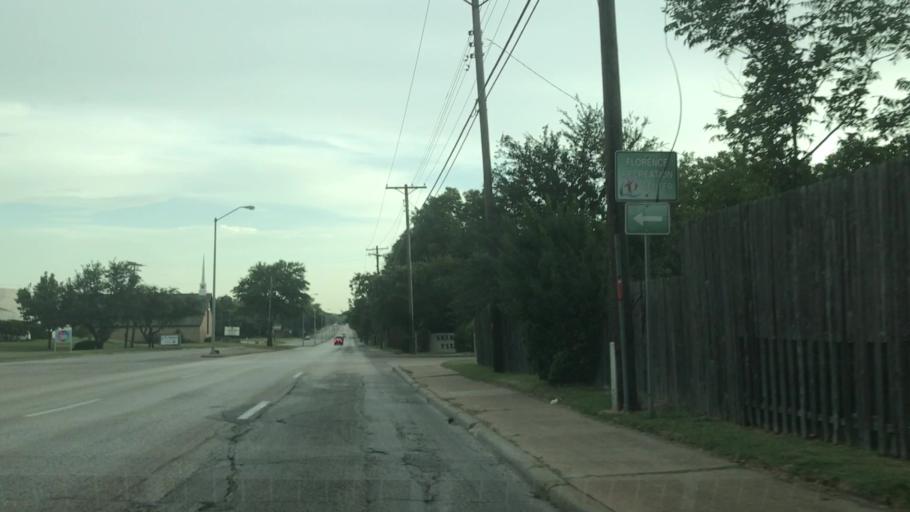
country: US
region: Texas
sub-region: Dallas County
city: Mesquite
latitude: 32.8316
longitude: -96.6367
